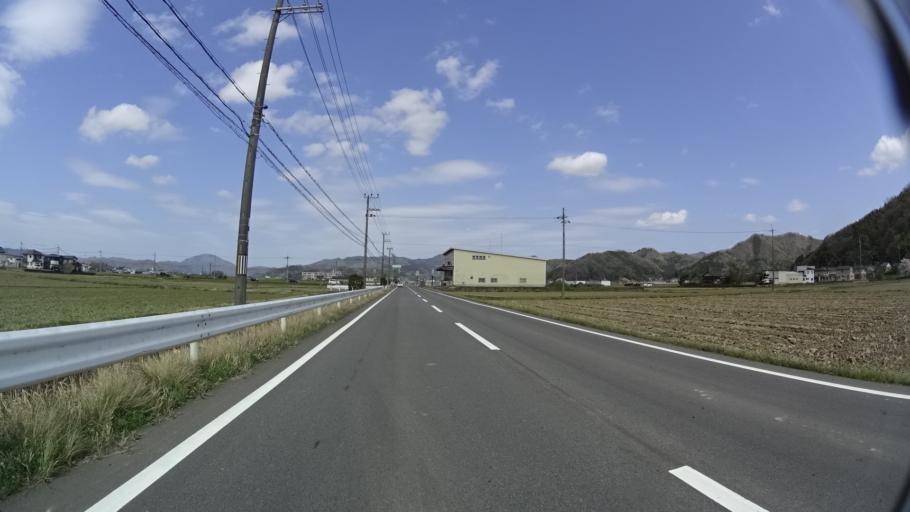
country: JP
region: Hyogo
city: Toyooka
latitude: 35.5228
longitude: 134.8399
